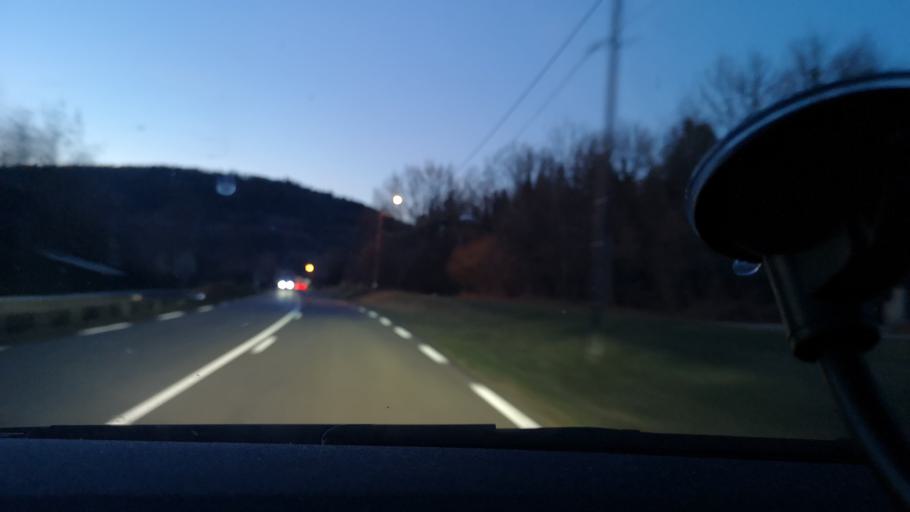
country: FR
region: Franche-Comte
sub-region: Departement du Jura
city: Champagnole
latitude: 46.7570
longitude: 5.9461
